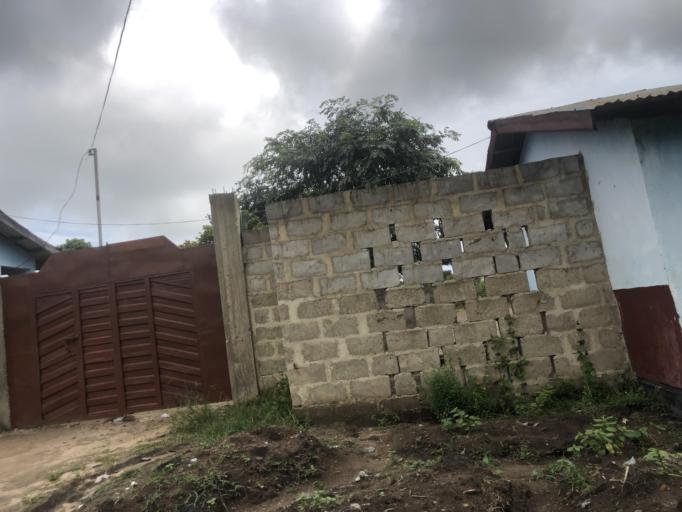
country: SL
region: Northern Province
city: Makeni
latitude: 8.9087
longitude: -12.0436
